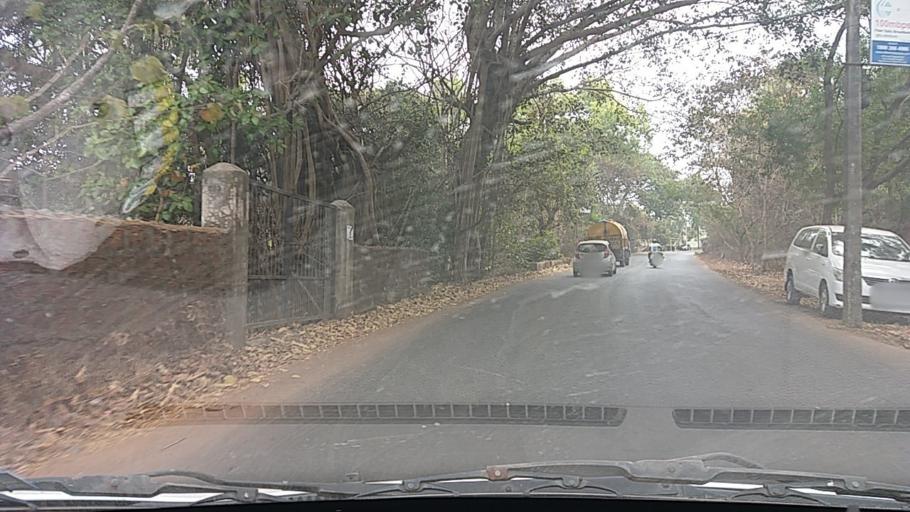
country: IN
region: Goa
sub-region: North Goa
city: Saligao
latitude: 15.5394
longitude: 73.7915
